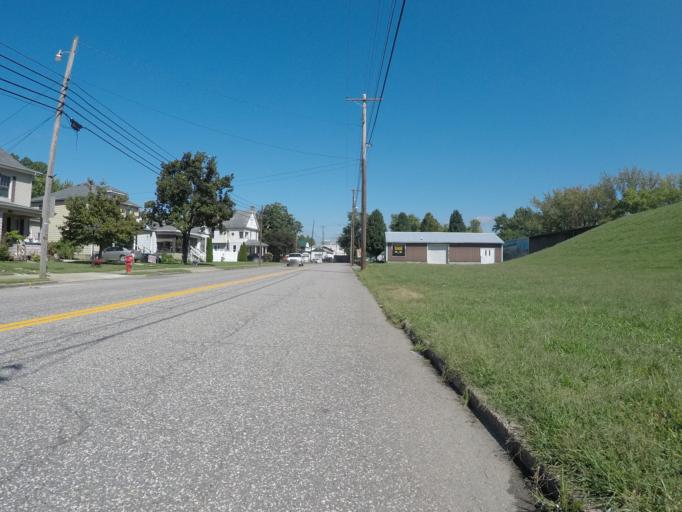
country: US
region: Kentucky
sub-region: Boyd County
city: Catlettsburg
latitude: 38.4121
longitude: -82.5980
